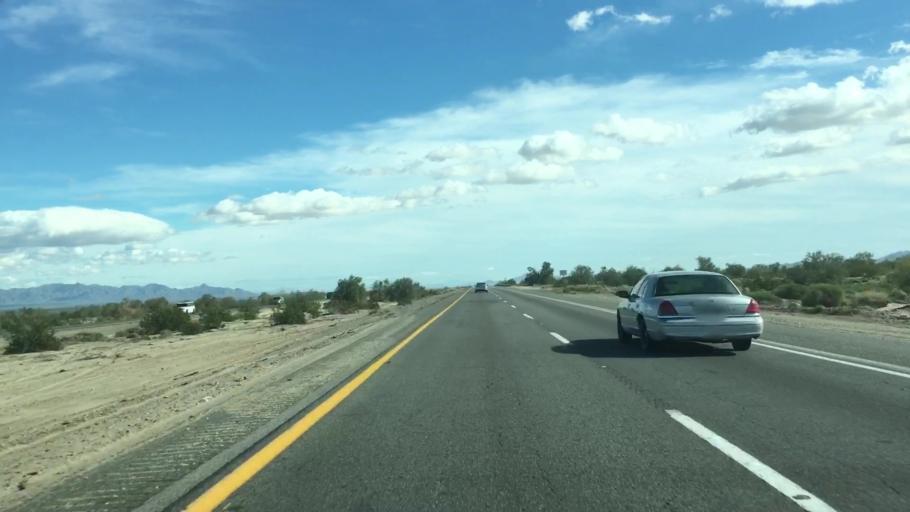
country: US
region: California
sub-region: Riverside County
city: Mesa Verde
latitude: 33.6637
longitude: -115.1805
